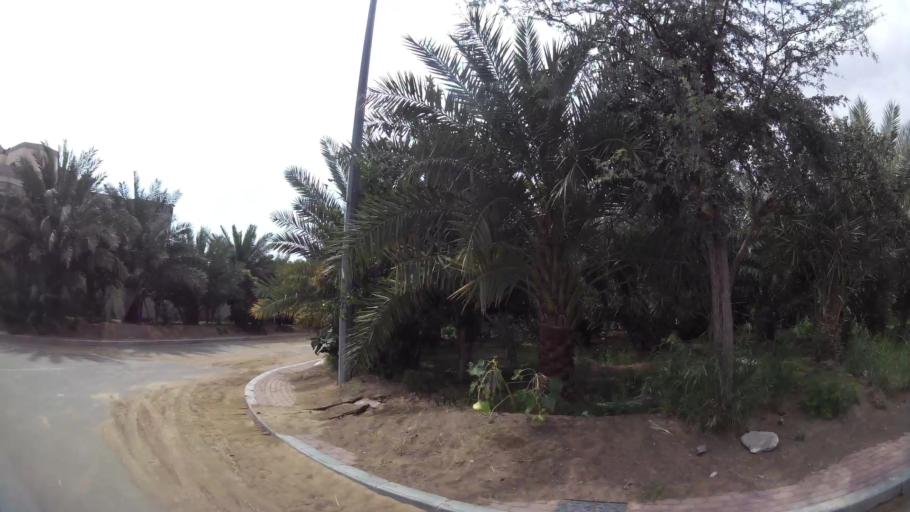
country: AE
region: Abu Dhabi
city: Al Ain
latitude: 24.1910
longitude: 55.8110
